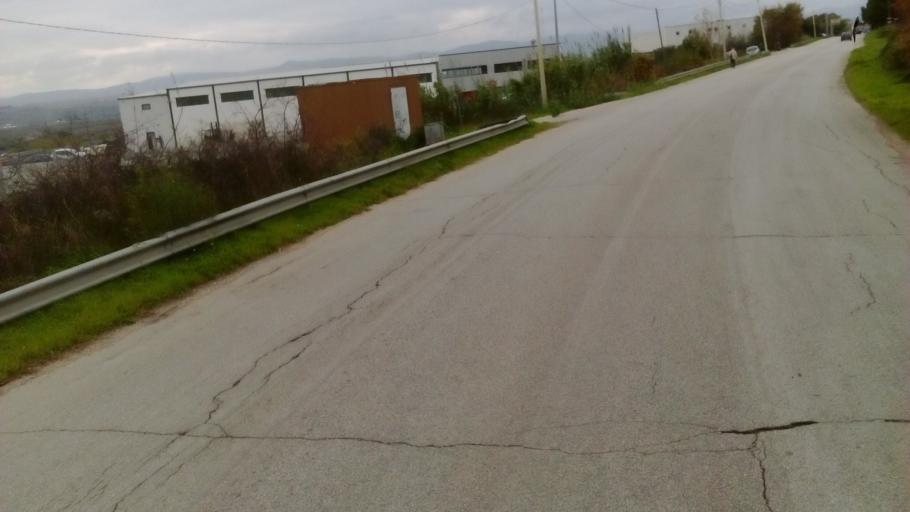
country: IT
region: Abruzzo
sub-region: Provincia di Chieti
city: San Salvo
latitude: 42.0434
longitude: 14.7535
